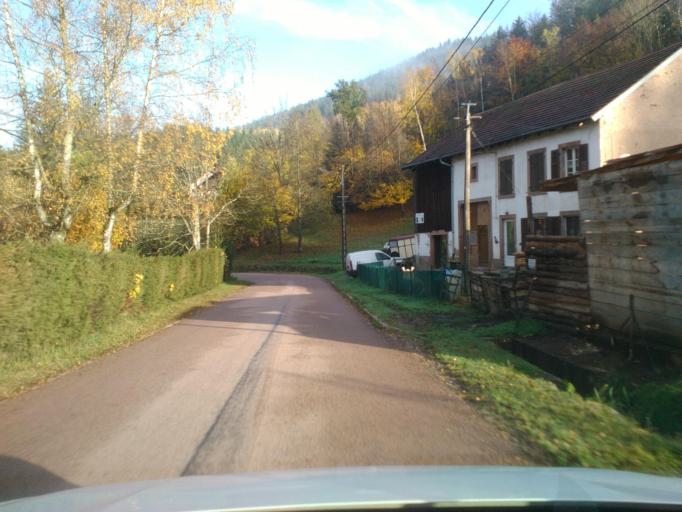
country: FR
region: Lorraine
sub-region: Departement des Vosges
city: Senones
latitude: 48.4227
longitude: 7.0383
